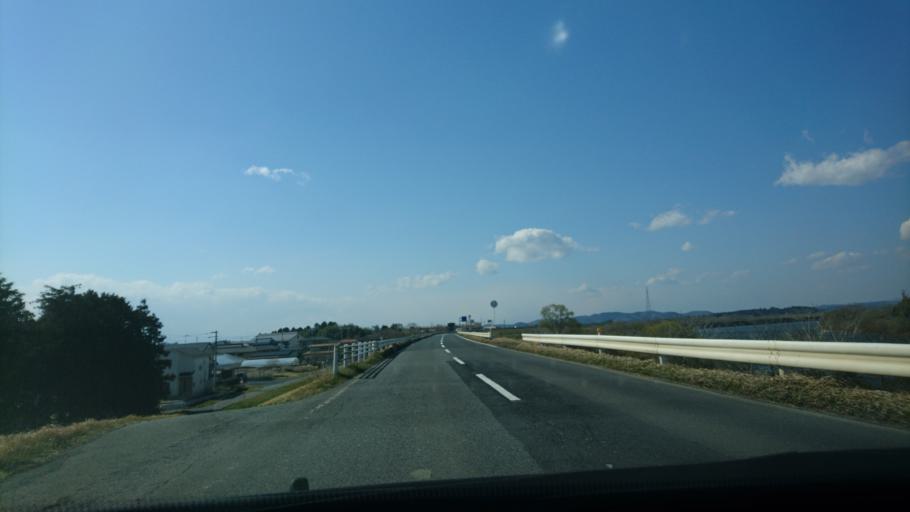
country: JP
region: Miyagi
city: Wakuya
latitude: 38.7054
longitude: 141.2709
